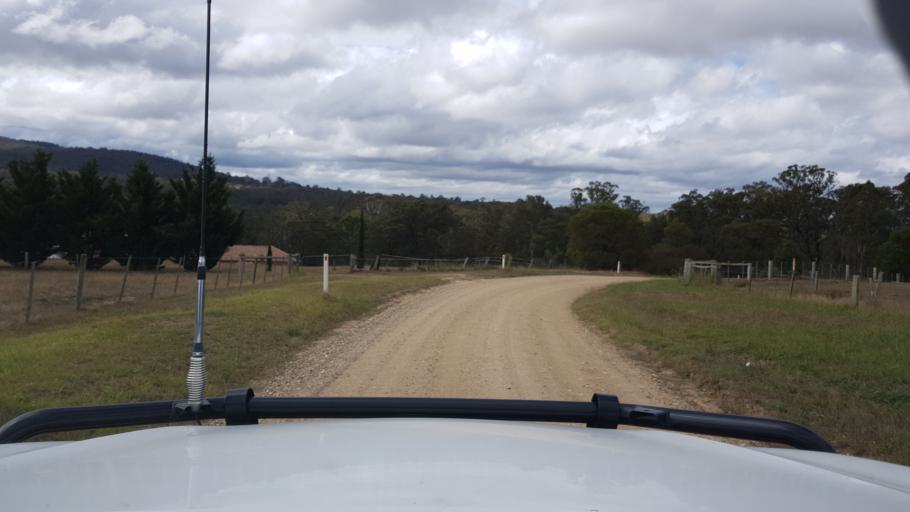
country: AU
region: Victoria
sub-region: East Gippsland
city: Bairnsdale
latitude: -37.7838
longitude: 147.5274
